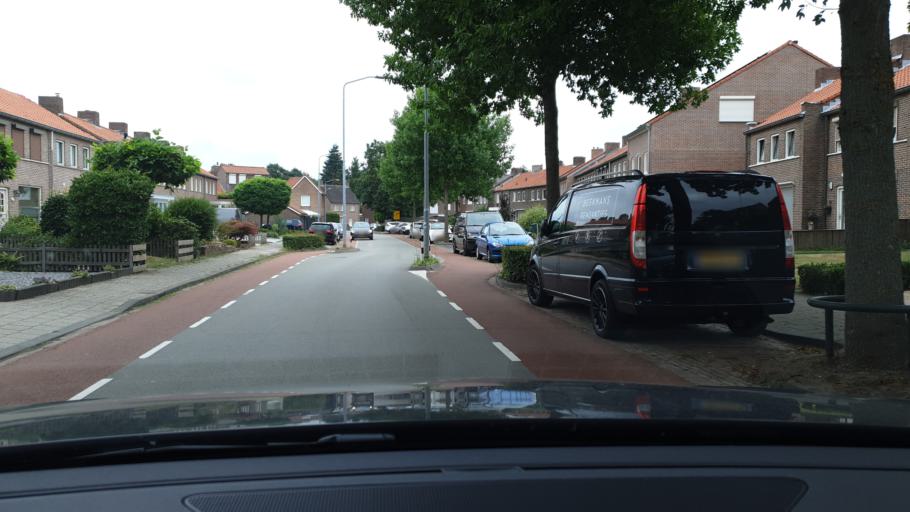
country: NL
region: North Brabant
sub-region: Gemeente Veldhoven
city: Veldhoven
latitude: 51.4265
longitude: 5.4181
